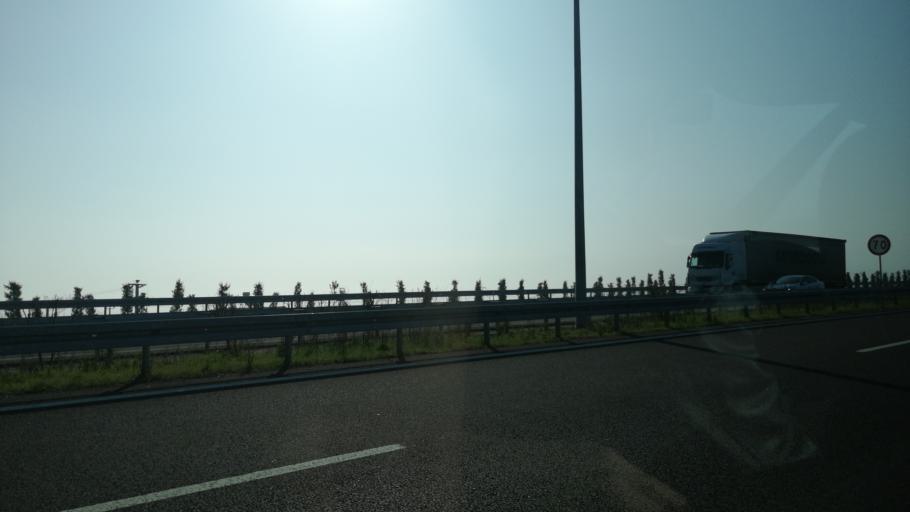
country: TR
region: Yalova
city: Altinova
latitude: 40.7204
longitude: 29.5022
